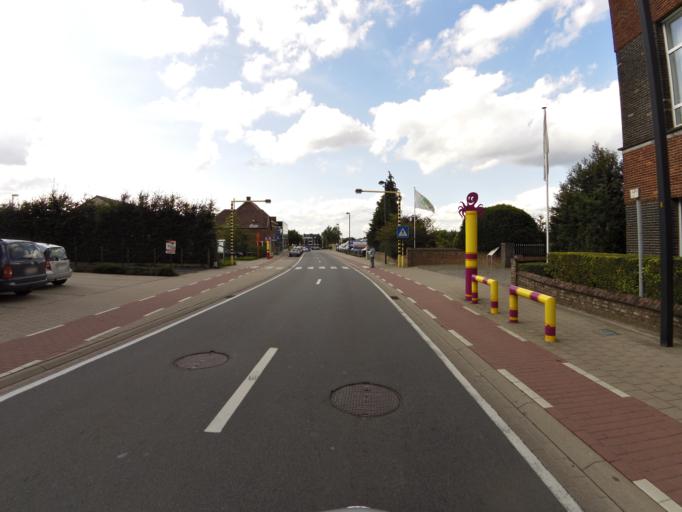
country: BE
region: Flanders
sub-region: Provincie West-Vlaanderen
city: Anzegem
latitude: 50.8393
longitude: 3.4739
